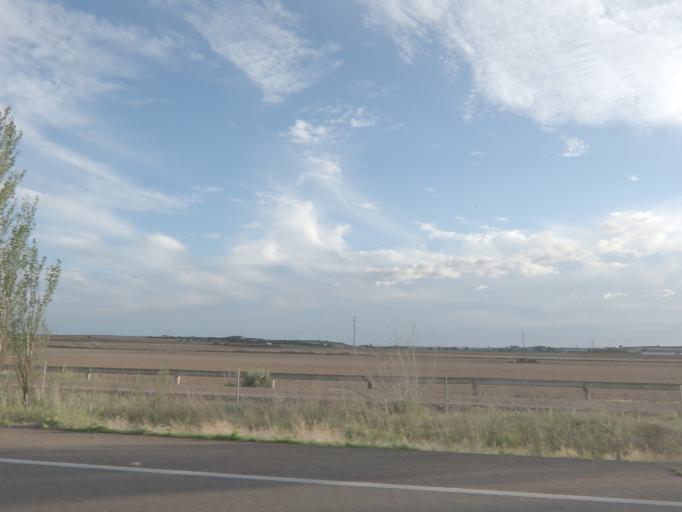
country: ES
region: Extremadura
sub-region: Provincia de Badajoz
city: Talavera La Real
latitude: 38.8638
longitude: -6.7535
